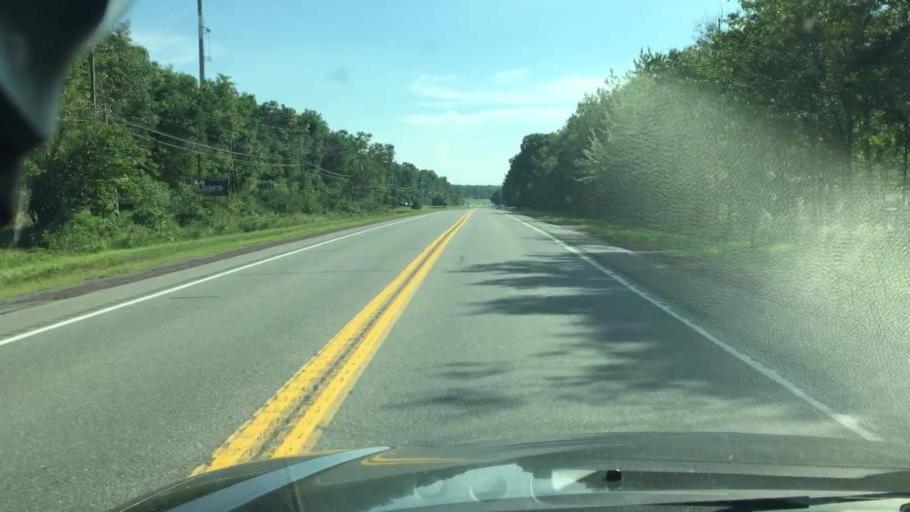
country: US
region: Pennsylvania
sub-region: Carbon County
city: Towamensing Trails
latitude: 40.9420
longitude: -75.6548
